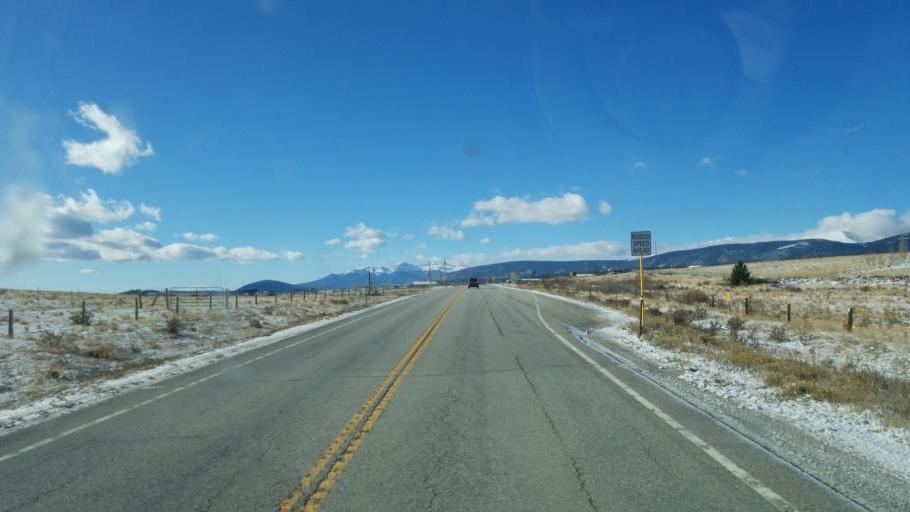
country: US
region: Colorado
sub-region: Park County
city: Fairplay
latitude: 39.2336
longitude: -105.9857
